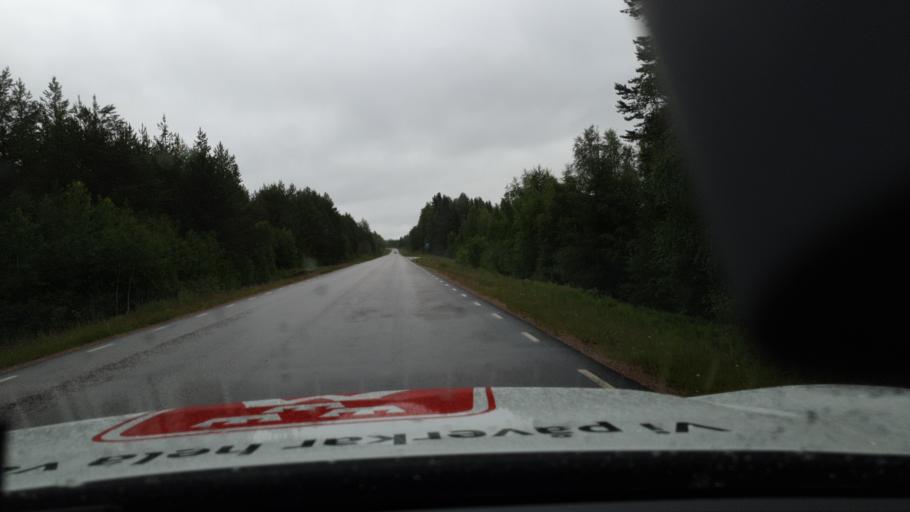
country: SE
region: Norrbotten
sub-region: Overtornea Kommun
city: OEvertornea
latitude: 66.4741
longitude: 23.6796
